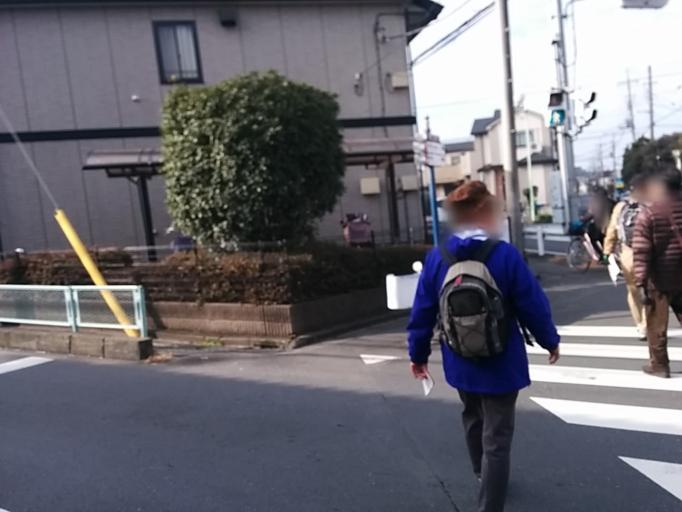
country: JP
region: Saitama
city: Kawagoe
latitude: 35.9112
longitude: 139.4914
